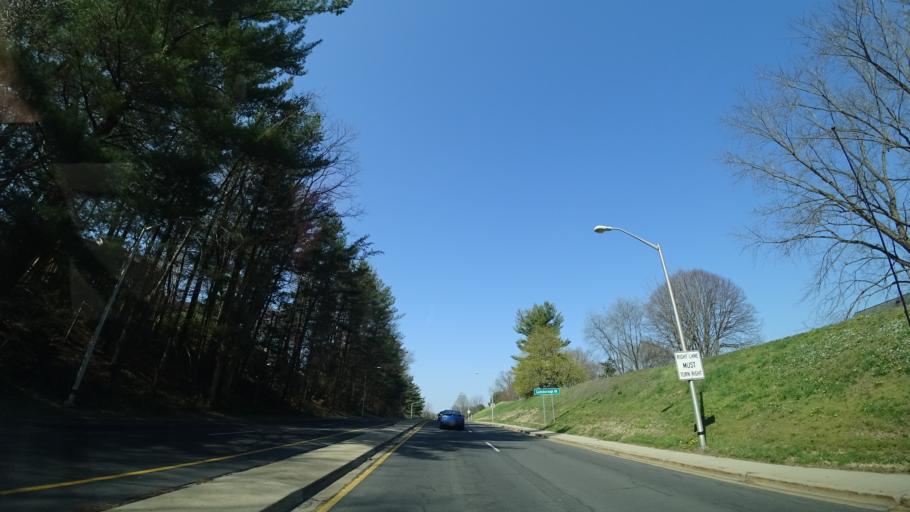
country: US
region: Maryland
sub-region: Montgomery County
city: Potomac
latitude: 39.0231
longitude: -77.1646
